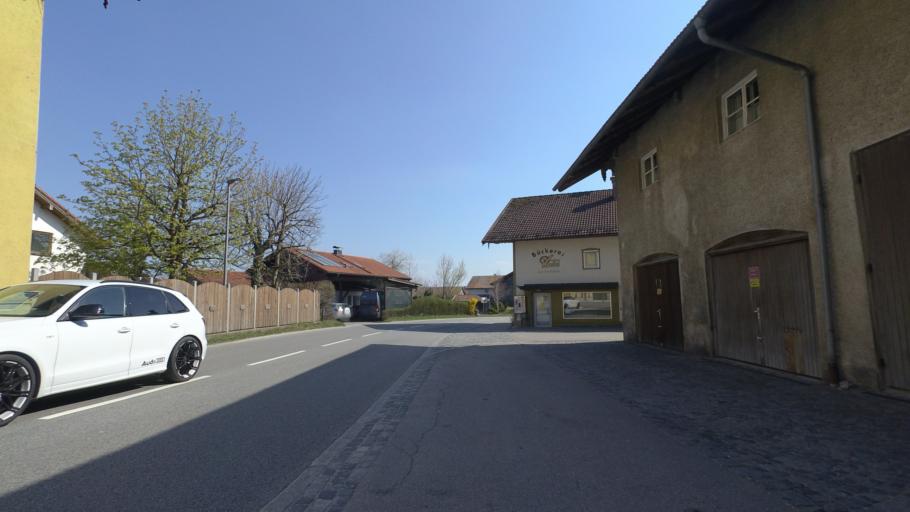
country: DE
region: Bavaria
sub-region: Upper Bavaria
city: Traunreut
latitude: 47.9367
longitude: 12.5936
